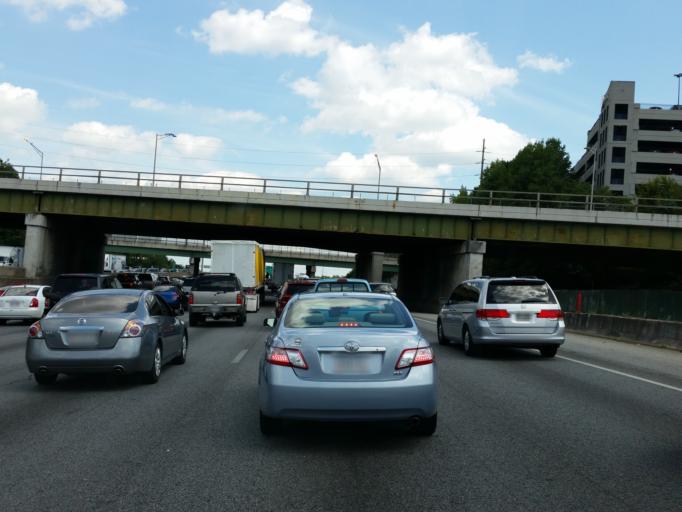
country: US
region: Georgia
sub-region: DeKalb County
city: Doraville
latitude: 33.9053
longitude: -84.2785
